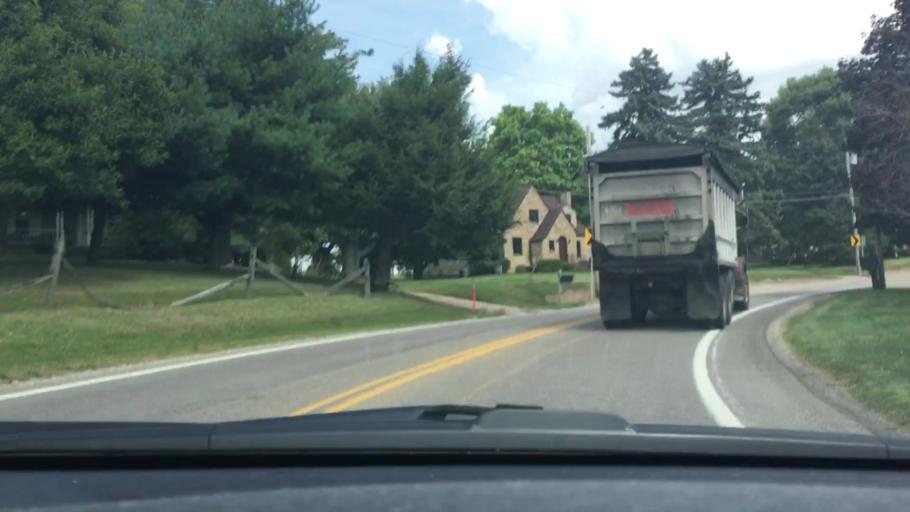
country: US
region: Pennsylvania
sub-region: Washington County
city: Gastonville
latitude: 40.2566
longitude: -79.9733
